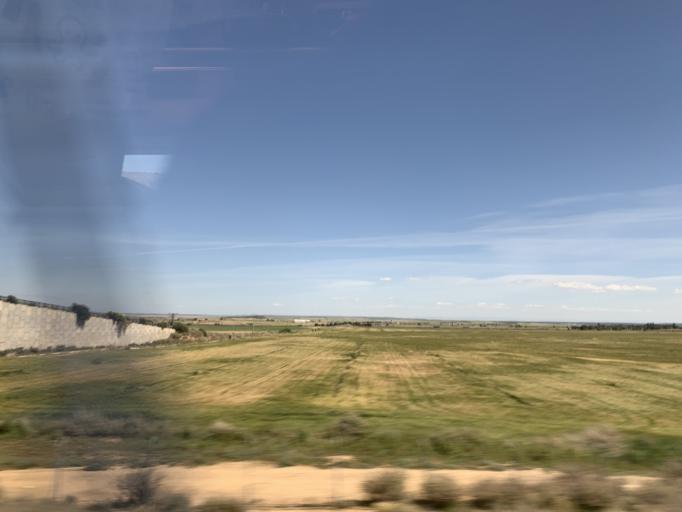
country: ES
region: Aragon
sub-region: Provincia de Huesca
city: Candasnos
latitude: 41.5334
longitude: 0.0433
